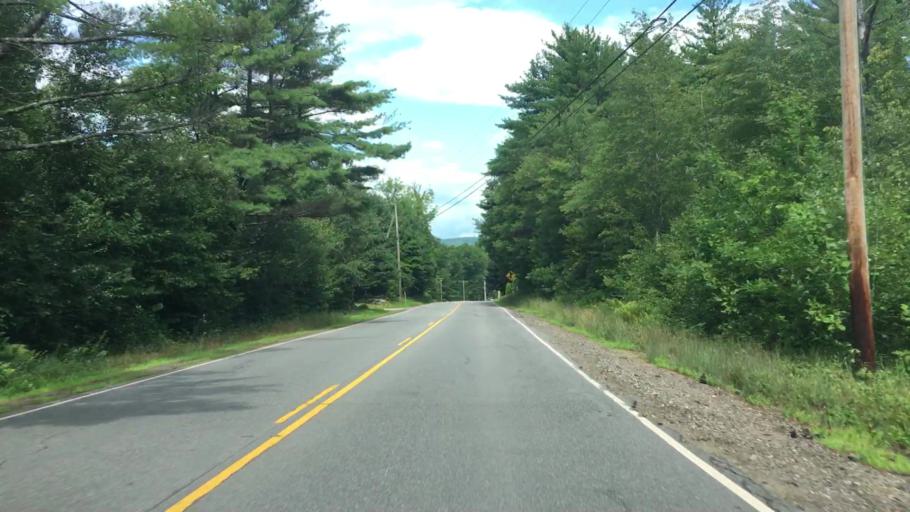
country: US
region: New Hampshire
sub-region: Belknap County
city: Meredith
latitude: 43.6041
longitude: -71.5222
